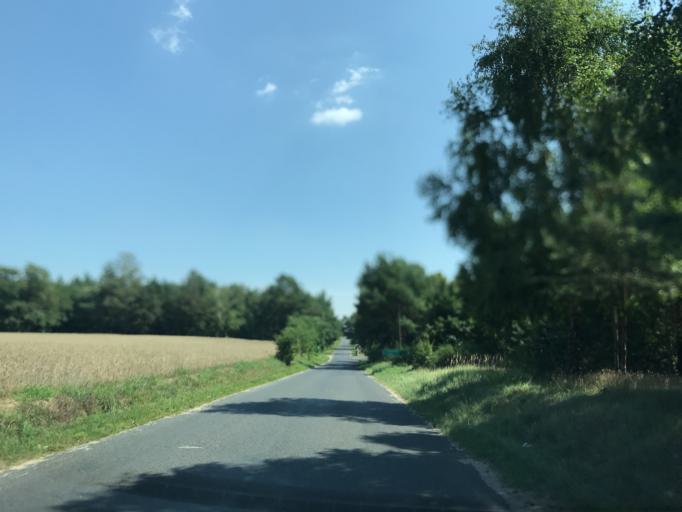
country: PL
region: Kujawsko-Pomorskie
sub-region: Powiat lipnowski
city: Chrostkowo
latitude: 52.9501
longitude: 19.2154
